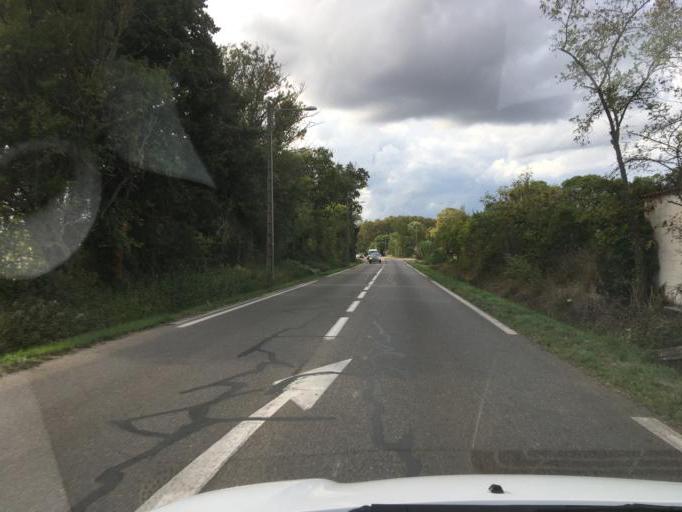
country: FR
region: Provence-Alpes-Cote d'Azur
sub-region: Departement du Vaucluse
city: Morieres-les-Avignon
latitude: 43.9433
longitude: 4.8861
